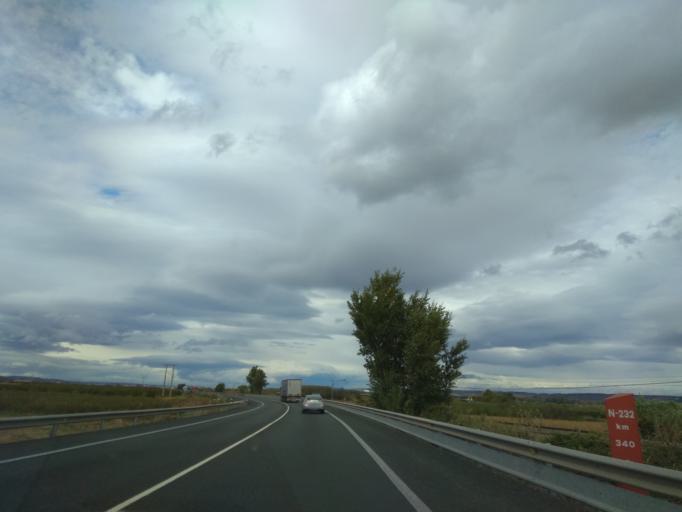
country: ES
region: La Rioja
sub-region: Provincia de La Rioja
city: Alfaro
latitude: 42.1989
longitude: -1.7765
